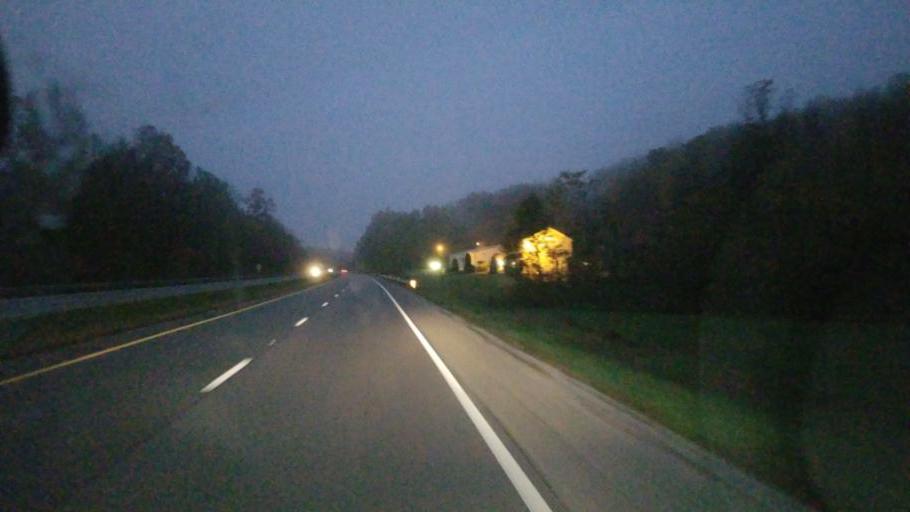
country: US
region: Ohio
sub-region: Ross County
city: Chillicothe
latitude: 39.2678
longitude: -82.9665
